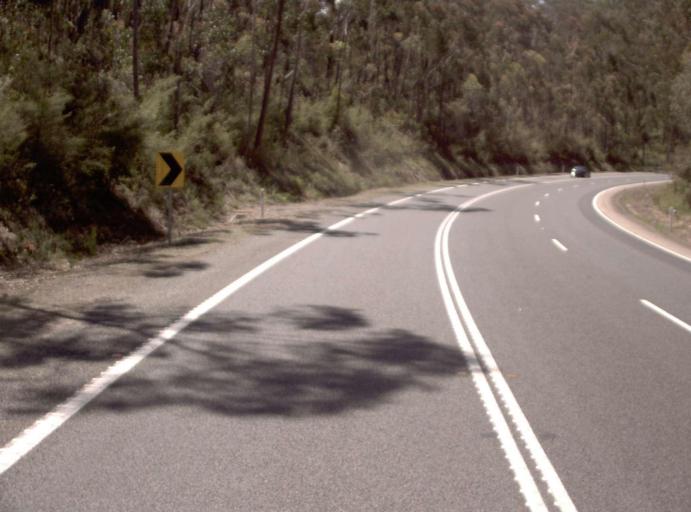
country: AU
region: New South Wales
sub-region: Bombala
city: Bombala
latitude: -37.6136
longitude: 148.8886
